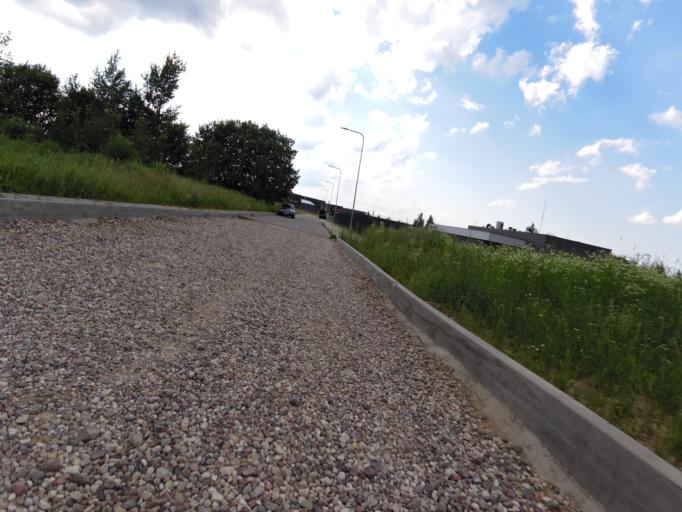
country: LT
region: Vilnius County
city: Pasilaiciai
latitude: 54.7513
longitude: 25.2190
